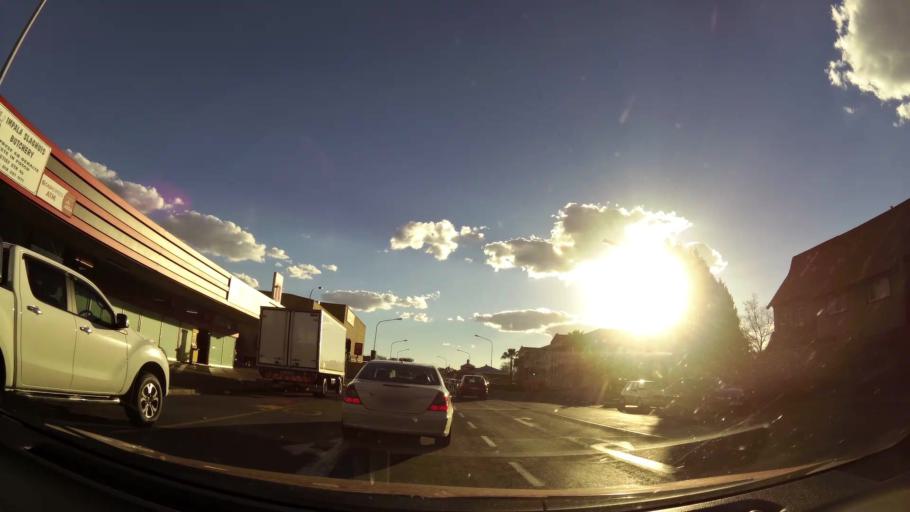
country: ZA
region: North-West
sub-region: Dr Kenneth Kaunda District Municipality
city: Potchefstroom
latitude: -26.7074
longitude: 27.0981
